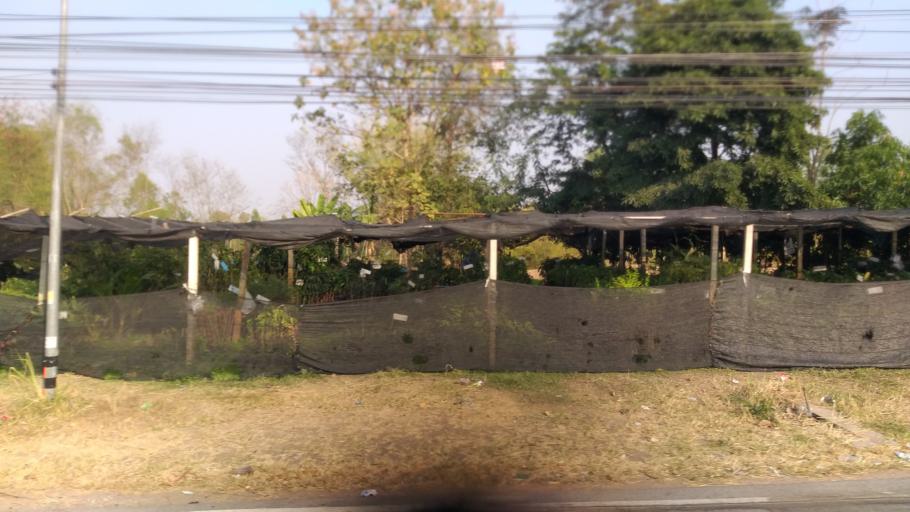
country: TH
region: Khon Kaen
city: Nam Phong
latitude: 16.6901
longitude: 102.8048
